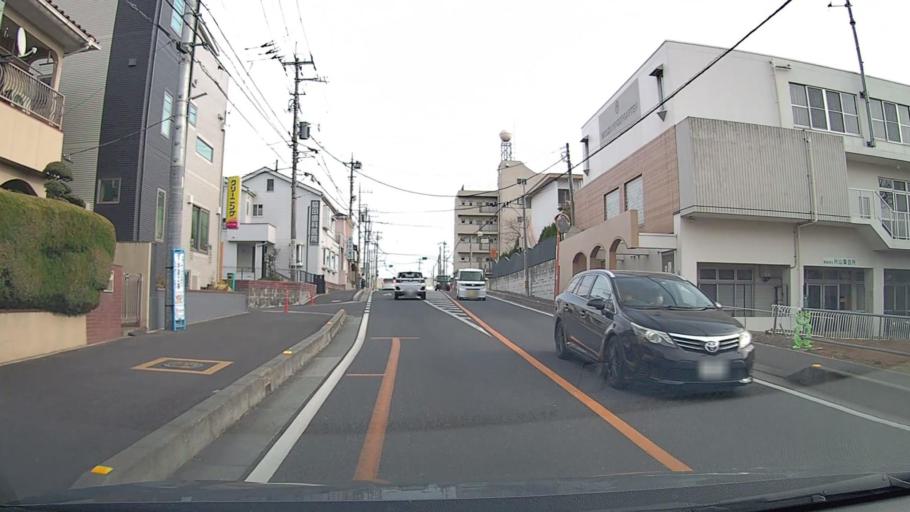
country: JP
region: Tokyo
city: Tanashicho
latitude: 35.7664
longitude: 139.5660
